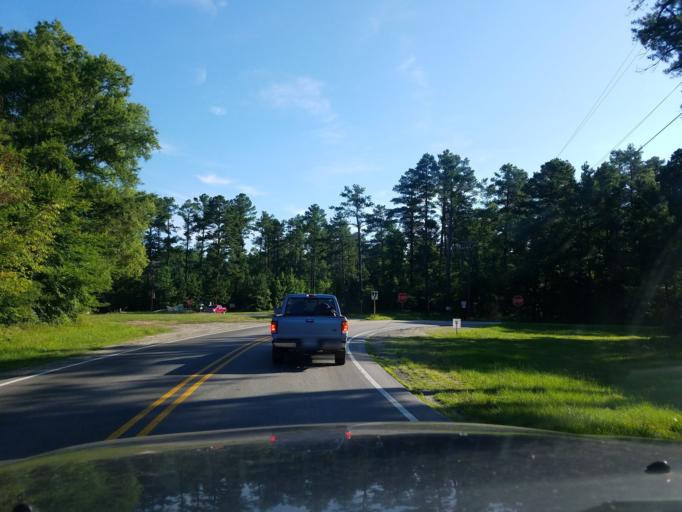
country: US
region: North Carolina
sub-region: Granville County
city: Butner
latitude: 36.1583
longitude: -78.7652
